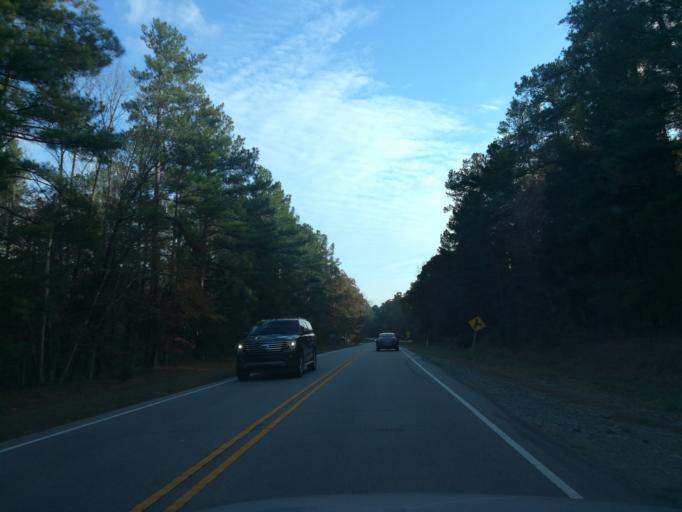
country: US
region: North Carolina
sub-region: Durham County
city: Durham
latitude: 36.0194
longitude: -78.9838
